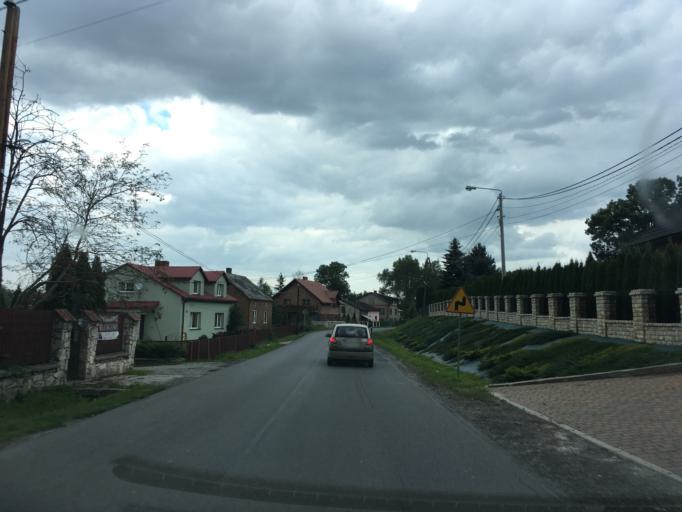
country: PL
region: Lesser Poland Voivodeship
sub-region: Powiat olkuski
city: Wolbrom
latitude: 50.3921
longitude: 19.7634
